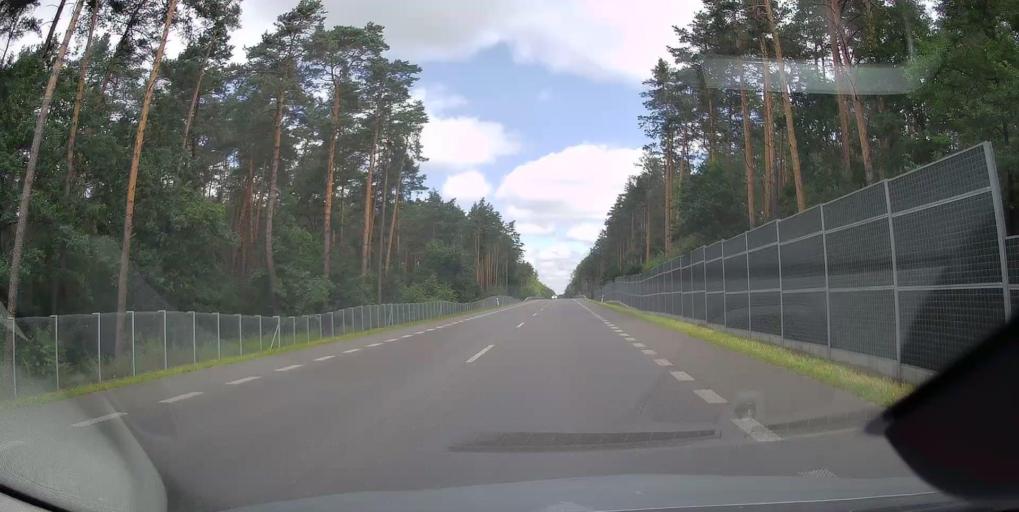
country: PL
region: Subcarpathian Voivodeship
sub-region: Powiat mielecki
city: Mielec
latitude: 50.2701
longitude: 21.4954
